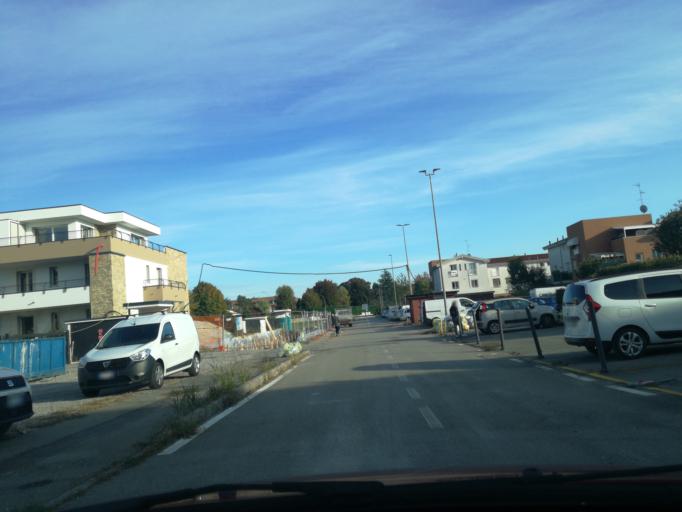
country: IT
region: Lombardy
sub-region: Provincia di Monza e Brianza
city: Bernareggio
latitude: 45.6480
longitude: 9.3977
